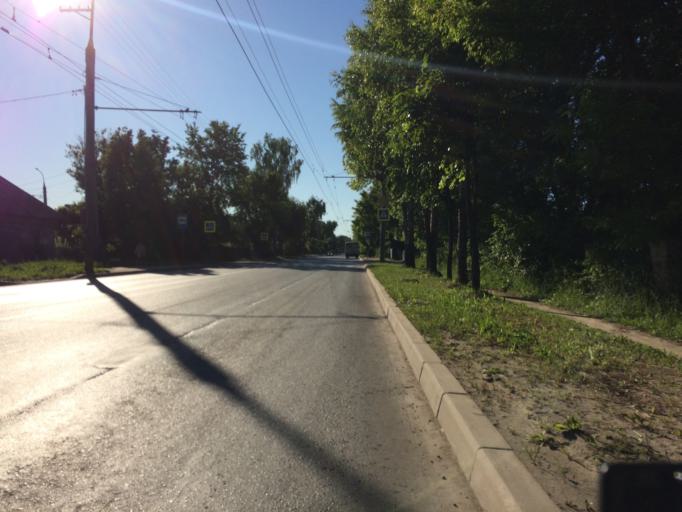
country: RU
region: Mariy-El
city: Yoshkar-Ola
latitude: 56.6515
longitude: 47.8881
